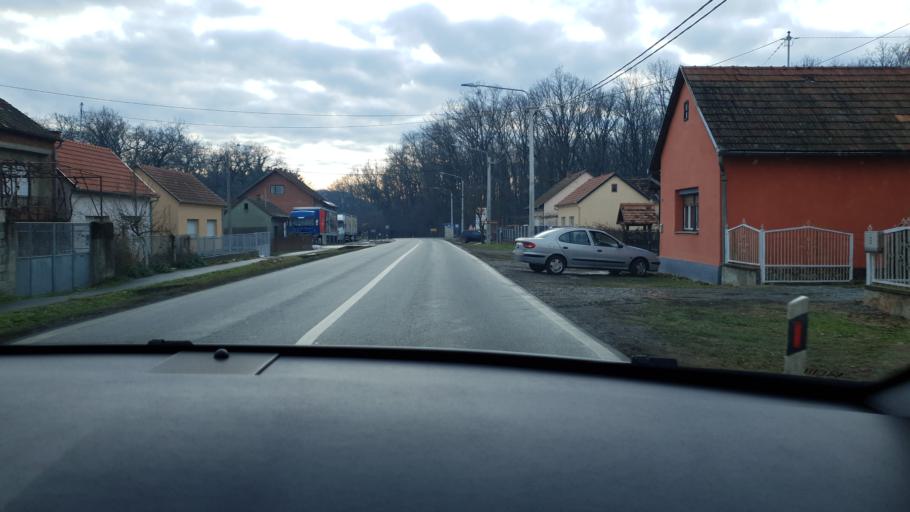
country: HR
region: Pozesko-Slavonska
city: Vidovci
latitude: 45.3517
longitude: 17.7229
